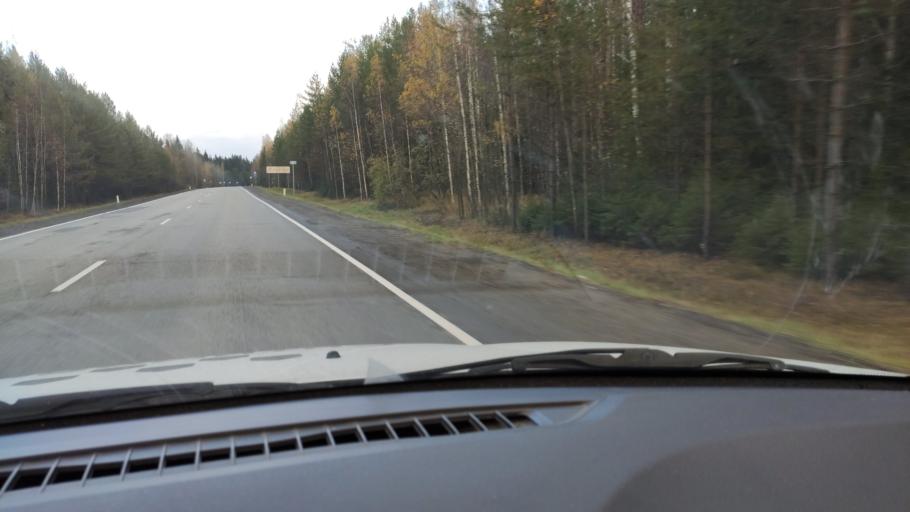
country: RU
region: Kirov
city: Belaya Kholunitsa
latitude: 58.9024
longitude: 50.9364
